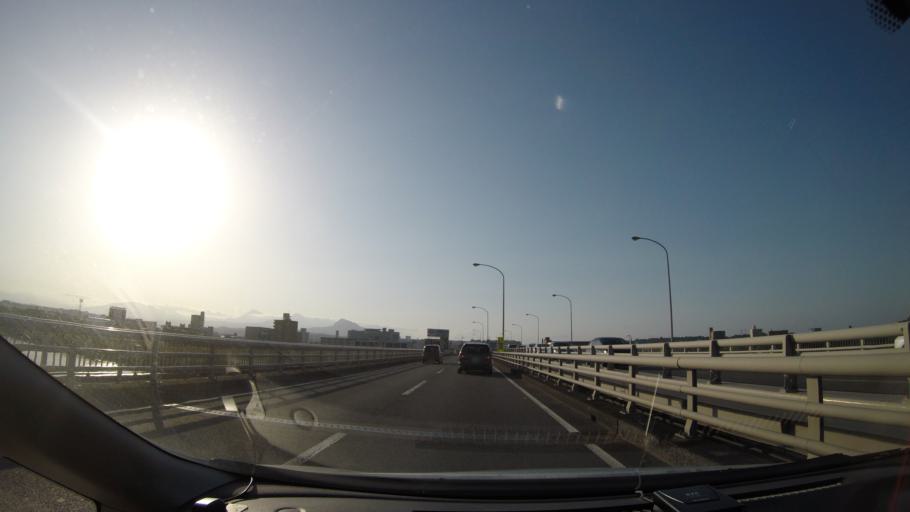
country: JP
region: Oita
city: Oita
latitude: 33.2020
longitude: 131.6058
